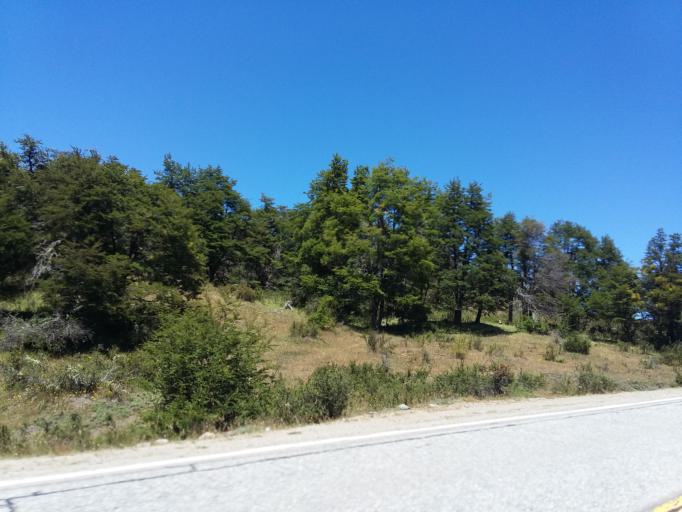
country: AR
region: Neuquen
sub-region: Departamento de Lacar
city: San Martin de los Andes
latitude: -40.2054
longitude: -71.3559
